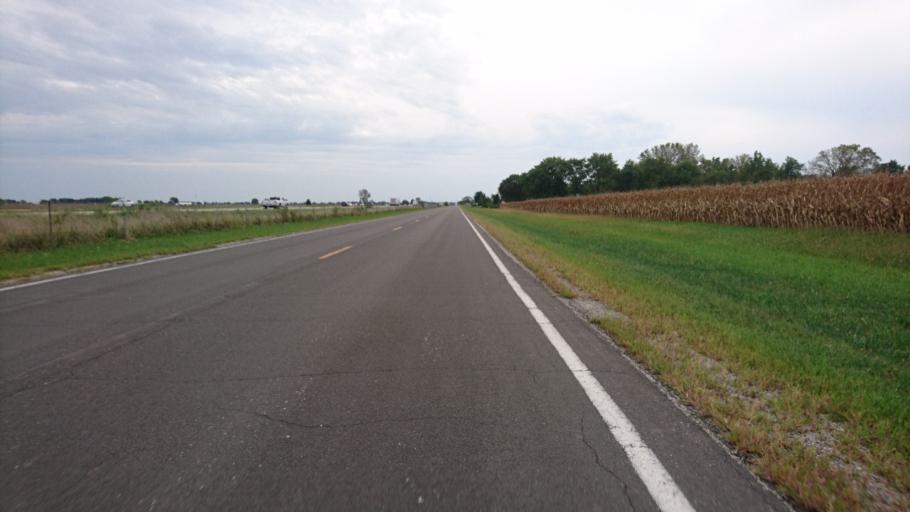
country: US
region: Illinois
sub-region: Sangamon County
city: Chatham
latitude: 39.6608
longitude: -89.6480
